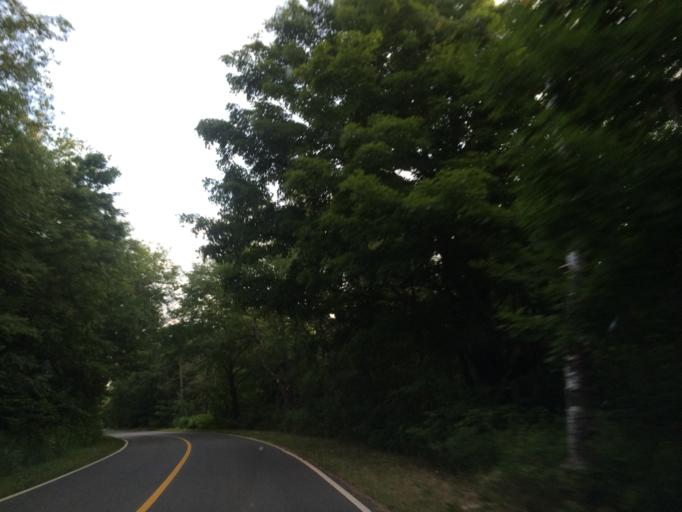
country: US
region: Massachusetts
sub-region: Berkshire County
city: Lanesborough
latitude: 42.5846
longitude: -73.2018
